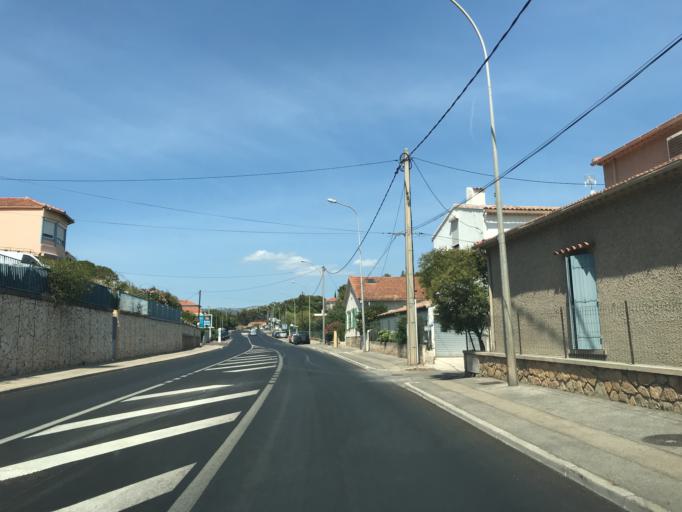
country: FR
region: Provence-Alpes-Cote d'Azur
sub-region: Departement du Var
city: La Seyne-sur-Mer
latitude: 43.0879
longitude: 5.8815
